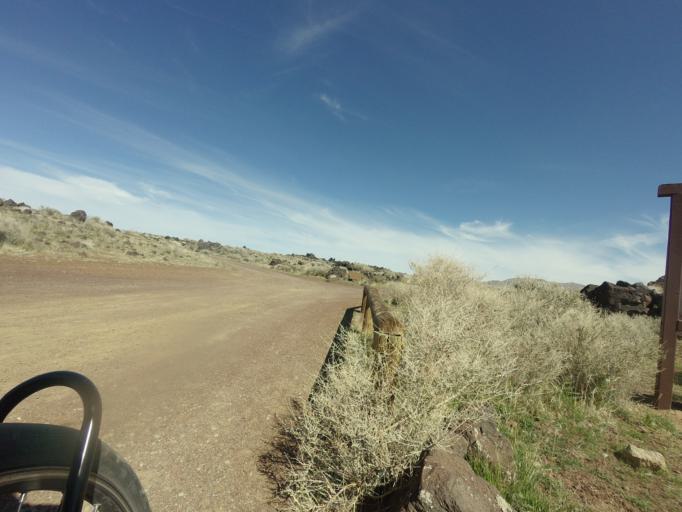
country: US
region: California
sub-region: Kern County
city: Inyokern
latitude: 35.9734
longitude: -117.9113
